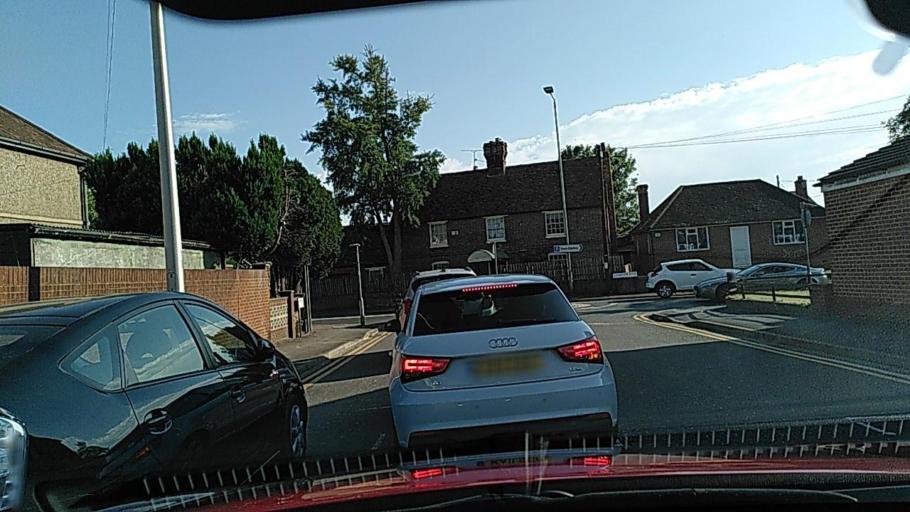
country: GB
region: England
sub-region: Reading
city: Reading
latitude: 51.4656
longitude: -0.9593
